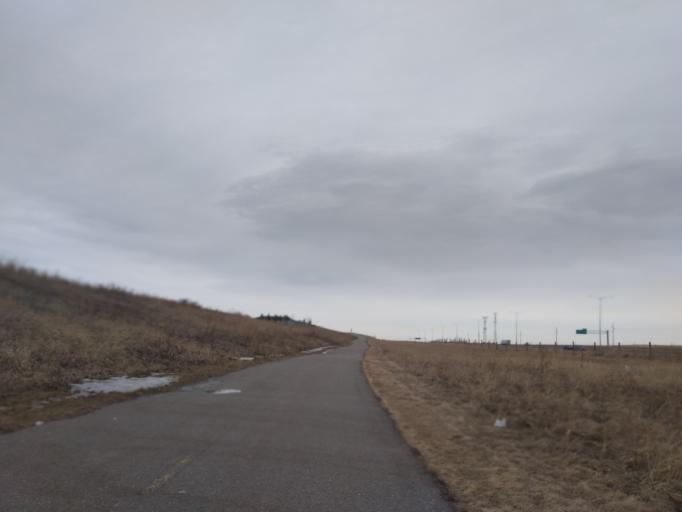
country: CA
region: Alberta
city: Chestermere
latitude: 51.1163
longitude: -113.9224
